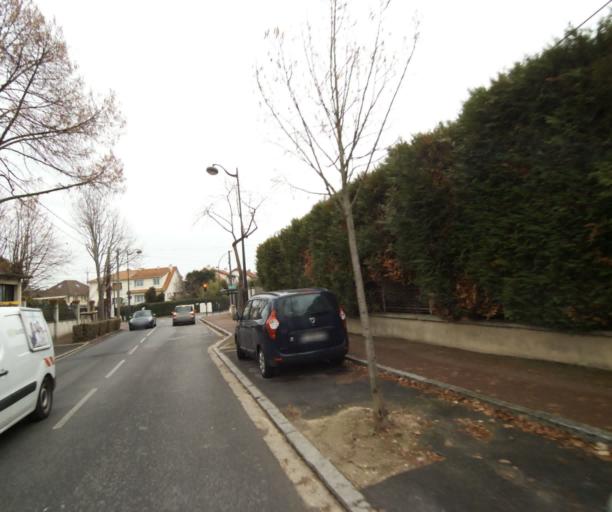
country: FR
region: Ile-de-France
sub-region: Departement des Hauts-de-Seine
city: Rueil-Malmaison
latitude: 48.8673
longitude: 2.1752
